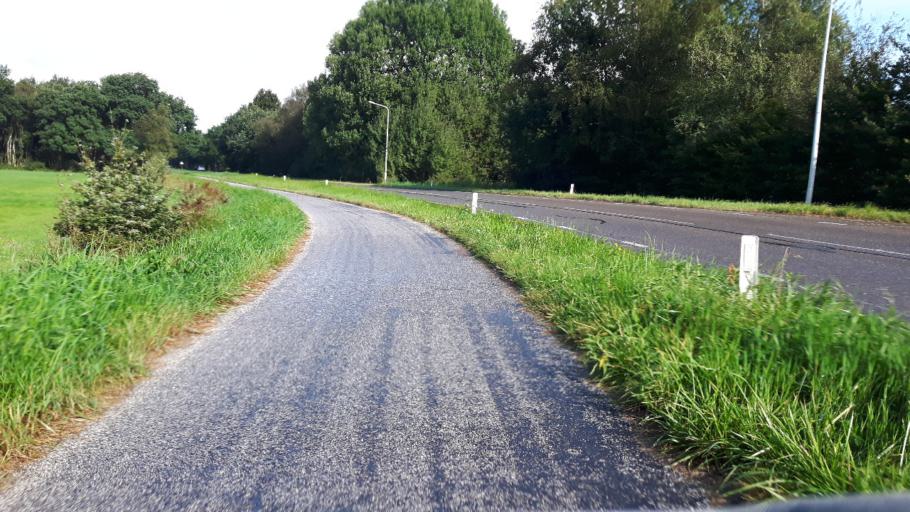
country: NL
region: Friesland
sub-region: Gemeente Smallingerland
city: Drachten
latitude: 53.0687
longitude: 6.1053
